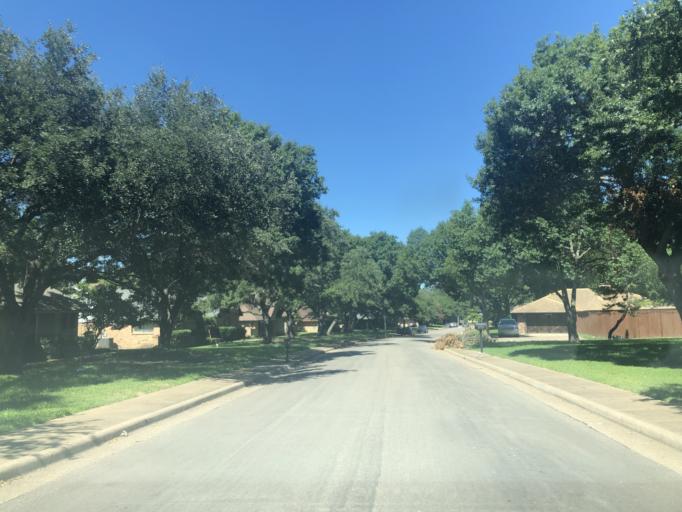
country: US
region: Texas
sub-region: Dallas County
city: Duncanville
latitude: 32.6456
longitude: -96.9360
